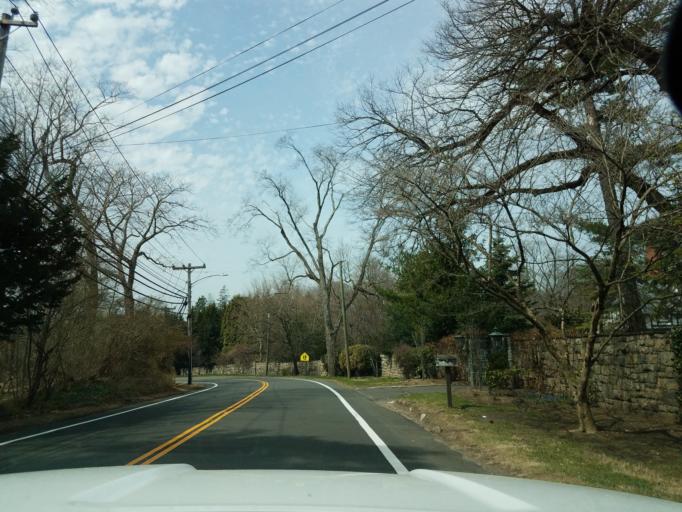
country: US
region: Connecticut
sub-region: Fairfield County
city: Greenwich
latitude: 41.0319
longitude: -73.6350
